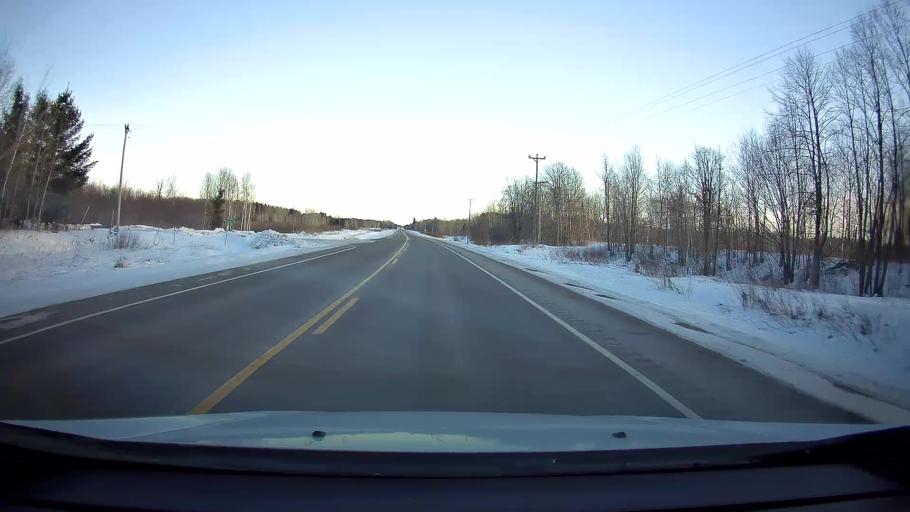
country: US
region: Wisconsin
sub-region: Washburn County
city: Shell Lake
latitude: 45.7104
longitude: -91.9442
